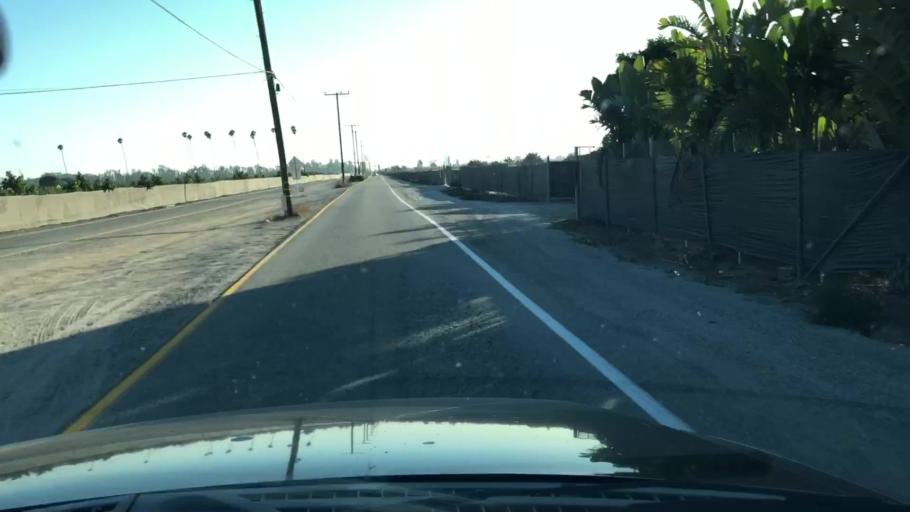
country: US
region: California
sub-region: Ventura County
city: Saticoy
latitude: 34.2634
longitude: -119.1291
